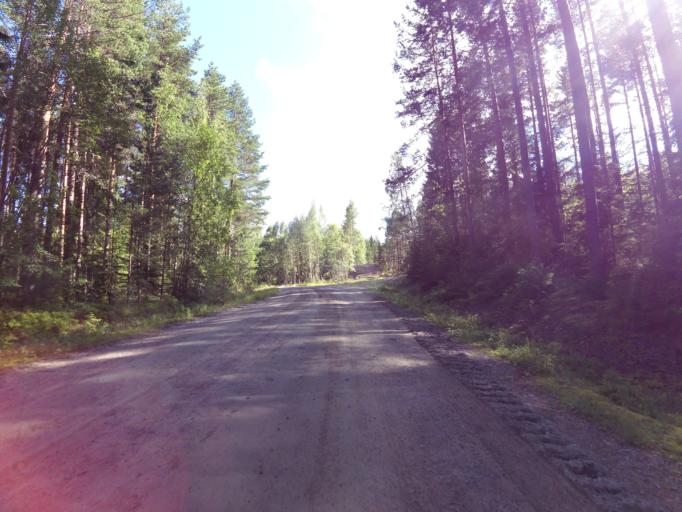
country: SE
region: Gaevleborg
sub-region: Hofors Kommun
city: Hofors
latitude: 60.5050
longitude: 16.3623
